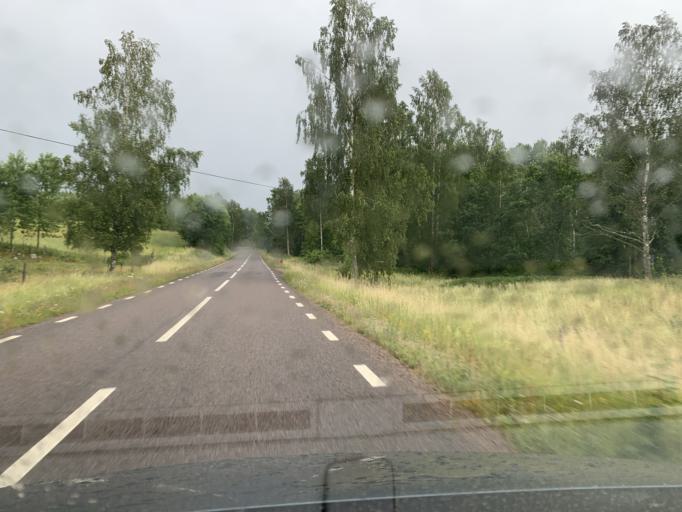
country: SE
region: Kalmar
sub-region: Vasterviks Kommun
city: Overum
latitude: 58.0082
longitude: 16.1728
